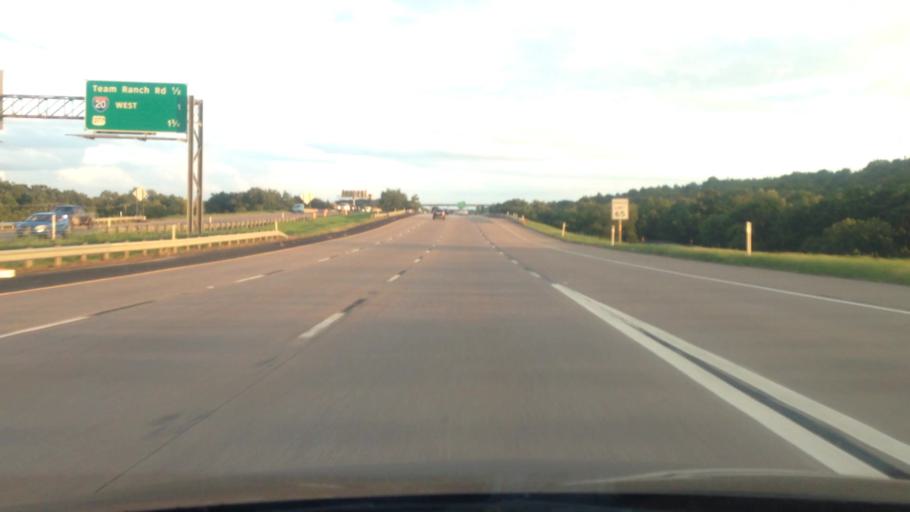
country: US
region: Texas
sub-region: Tarrant County
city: Benbrook
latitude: 32.7141
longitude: -97.4783
